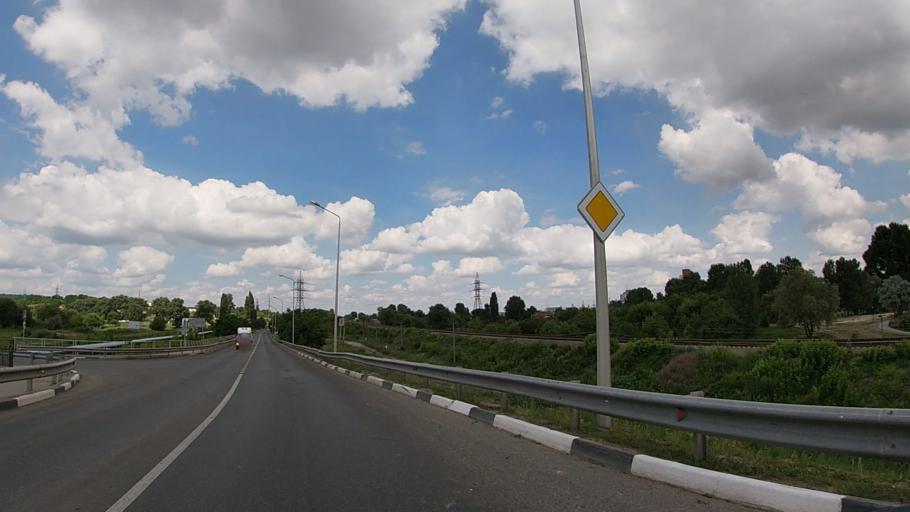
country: RU
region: Belgorod
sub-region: Belgorodskiy Rayon
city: Belgorod
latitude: 50.5911
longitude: 36.5648
